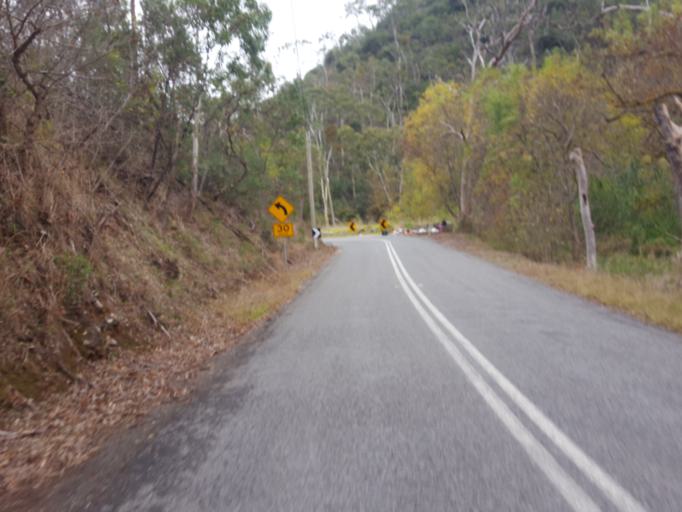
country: AU
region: South Australia
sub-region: Campbelltown
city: Athelstone
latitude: -34.8759
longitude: 138.7559
